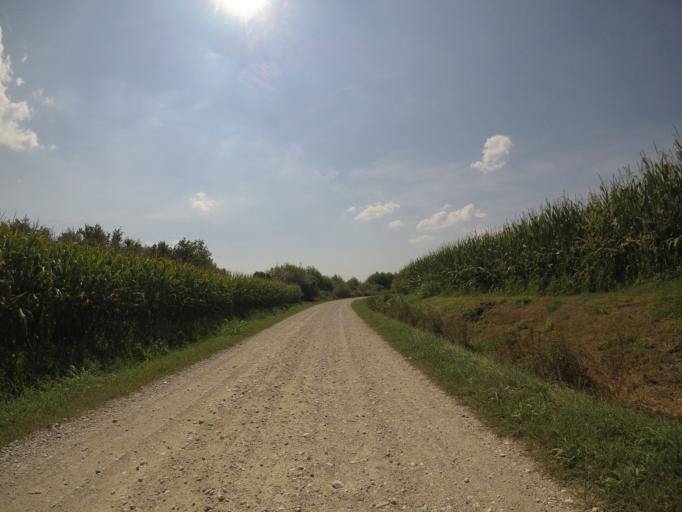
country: IT
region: Friuli Venezia Giulia
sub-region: Provincia di Udine
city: Bertiolo
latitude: 45.9299
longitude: 13.0706
